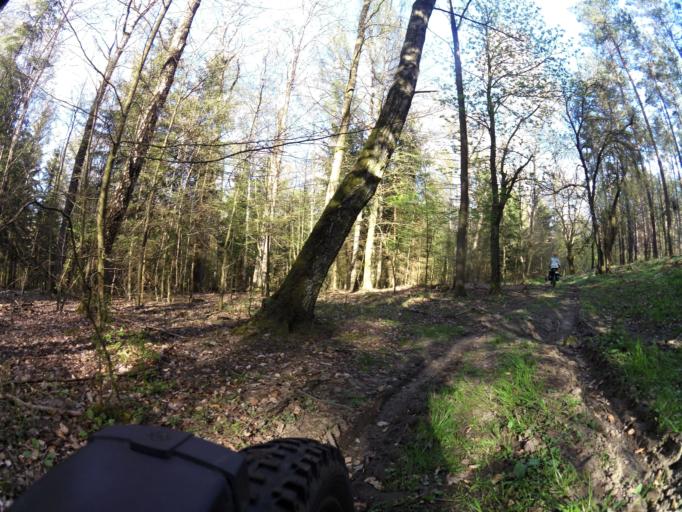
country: PL
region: West Pomeranian Voivodeship
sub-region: Powiat lobeski
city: Lobez
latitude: 53.7518
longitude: 15.6047
